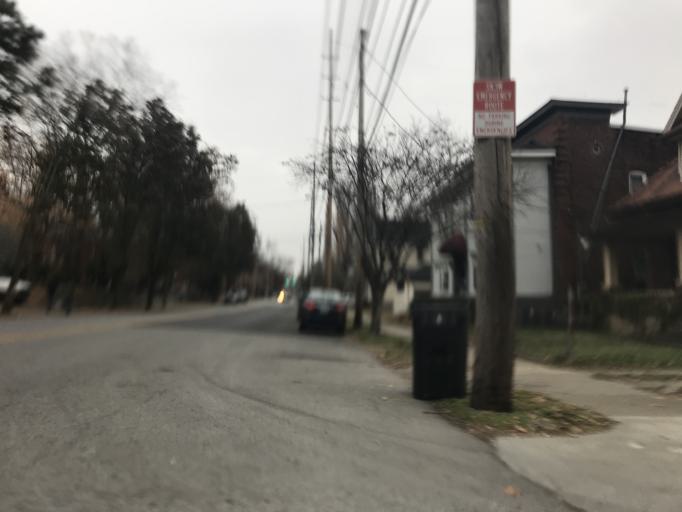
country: US
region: Indiana
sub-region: Clark County
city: Jeffersonville
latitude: 38.2554
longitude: -85.7124
